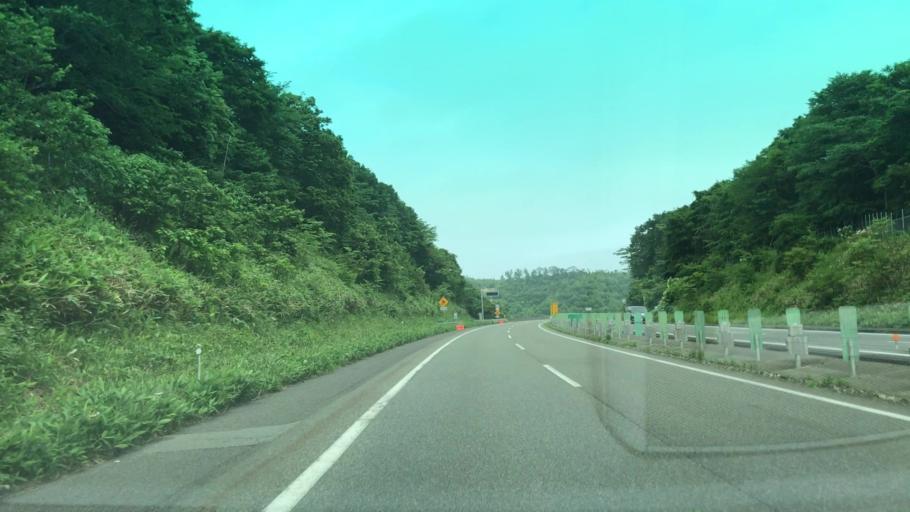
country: JP
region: Hokkaido
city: Shiraoi
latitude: 42.4929
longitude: 141.2407
